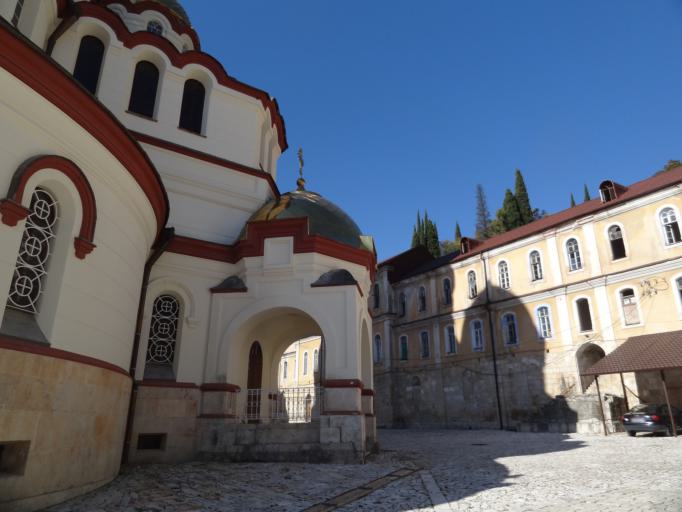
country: GE
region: Abkhazia
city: Stantsiya Novyy Afon
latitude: 43.0881
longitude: 40.8217
